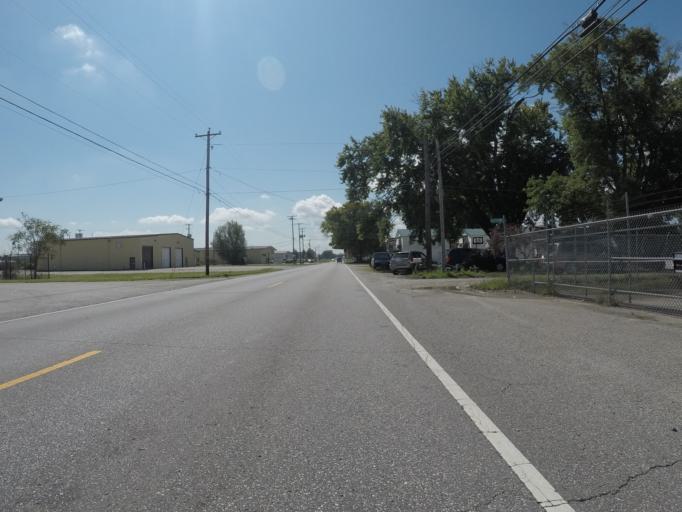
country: US
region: Ohio
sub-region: Lawrence County
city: South Point
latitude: 38.4401
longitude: -82.5945
